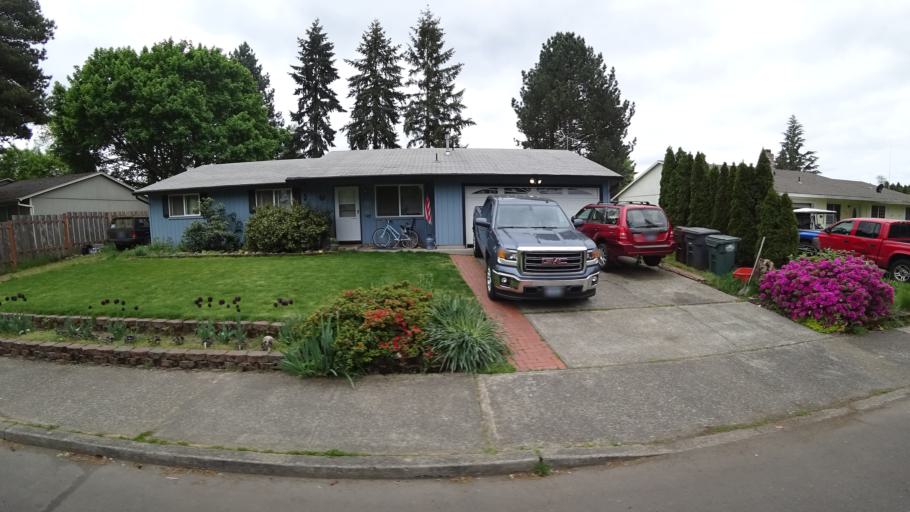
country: US
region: Oregon
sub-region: Washington County
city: Hillsboro
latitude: 45.5350
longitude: -122.9740
